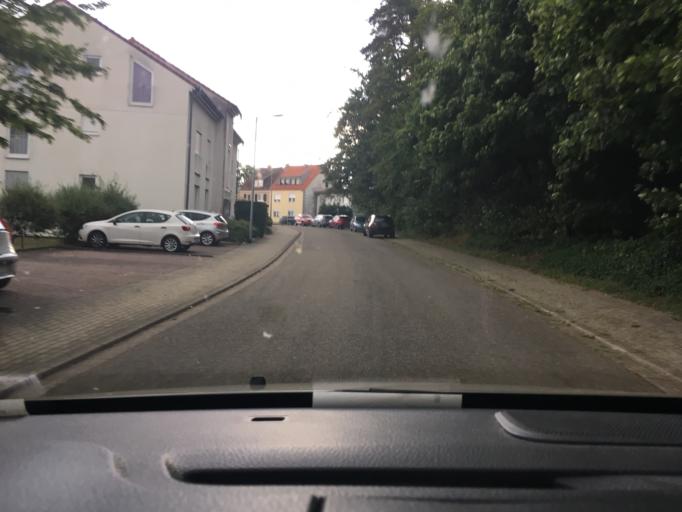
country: DE
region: Saarland
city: Sankt Ingbert
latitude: 49.2669
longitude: 7.1169
